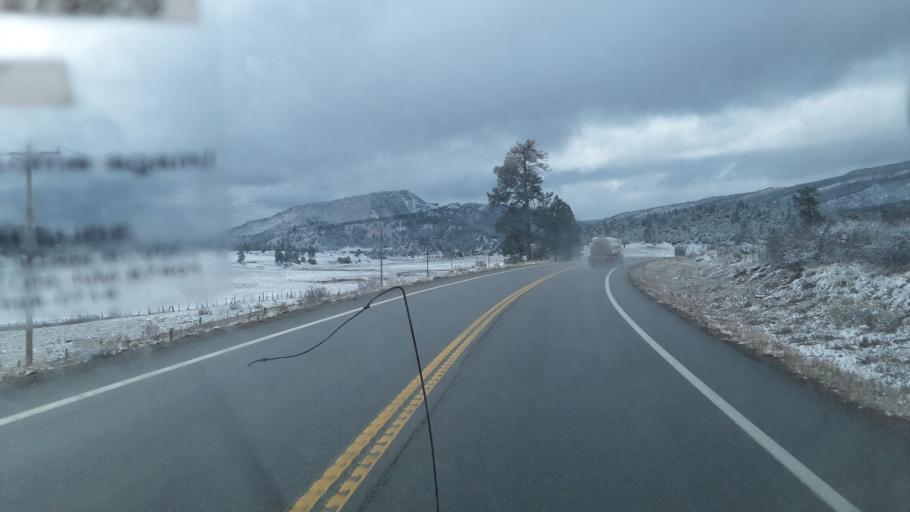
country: US
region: Colorado
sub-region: Archuleta County
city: Pagosa Springs
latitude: 37.2289
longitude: -107.1936
